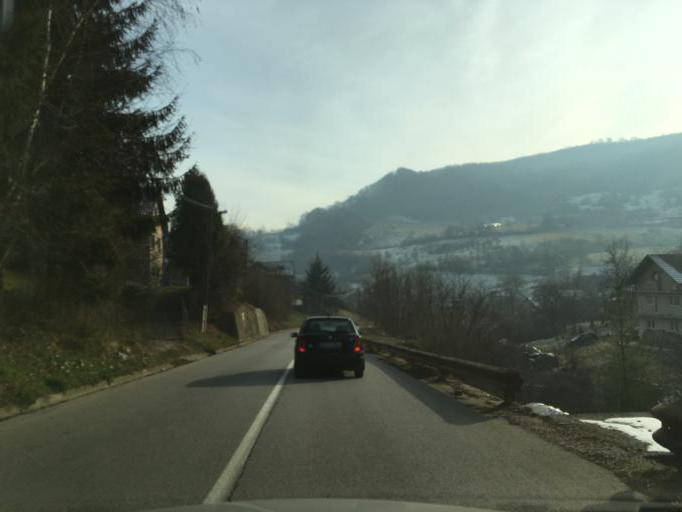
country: BA
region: Federation of Bosnia and Herzegovina
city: Lokvine
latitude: 44.1885
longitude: 17.8606
